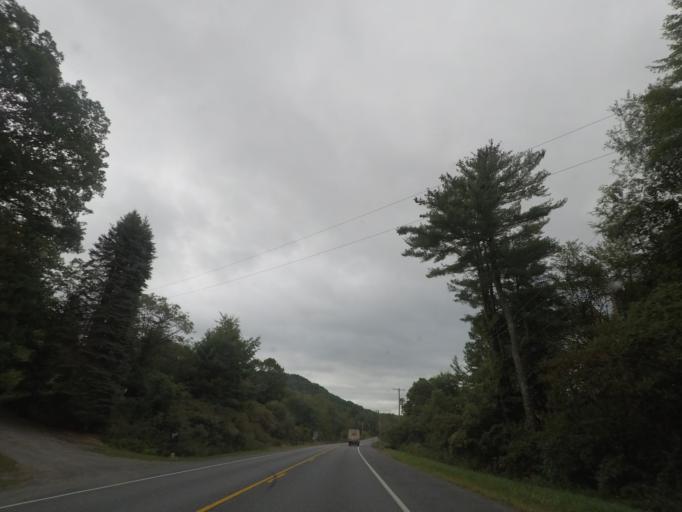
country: US
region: New York
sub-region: Rensselaer County
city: Hoosick Falls
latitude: 42.9454
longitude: -73.3694
